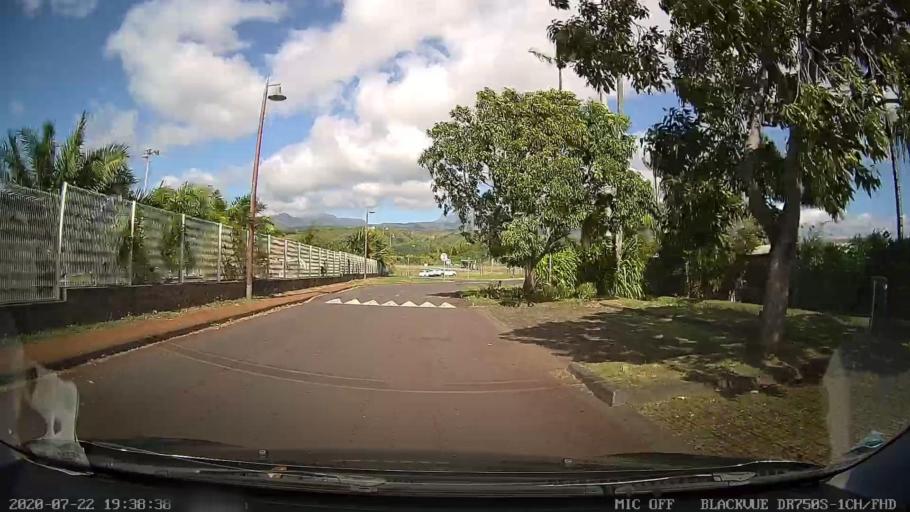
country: RE
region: Reunion
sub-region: Reunion
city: Sainte-Suzanne
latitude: -20.9129
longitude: 55.6145
